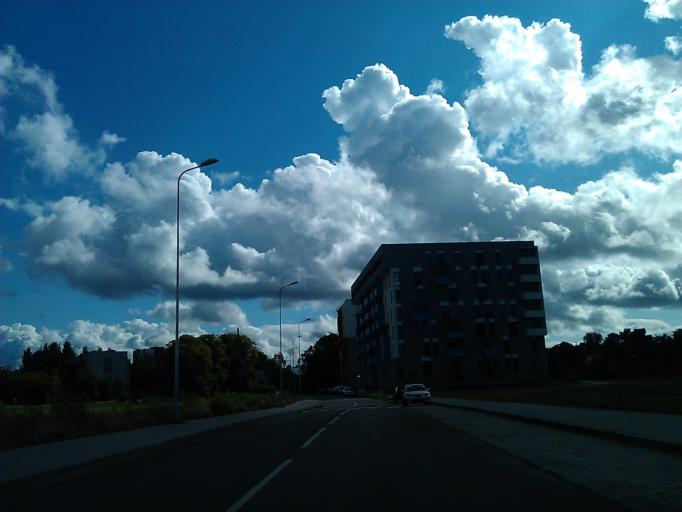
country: LV
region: Riga
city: Jaunciems
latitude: 56.9902
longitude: 24.1717
